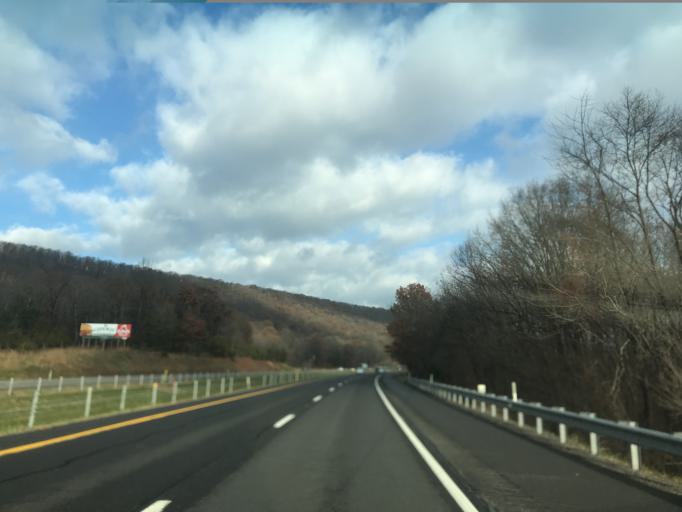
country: US
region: Maryland
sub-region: Washington County
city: Hancock
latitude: 39.8349
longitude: -78.2756
